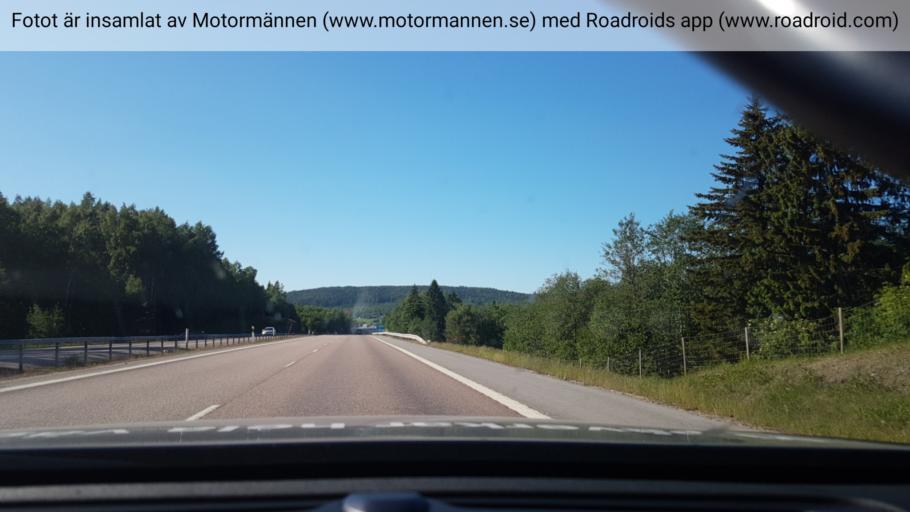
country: SE
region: Vaesternorrland
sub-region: Sundsvalls Kommun
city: Sundsbruk
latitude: 62.4330
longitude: 17.3427
